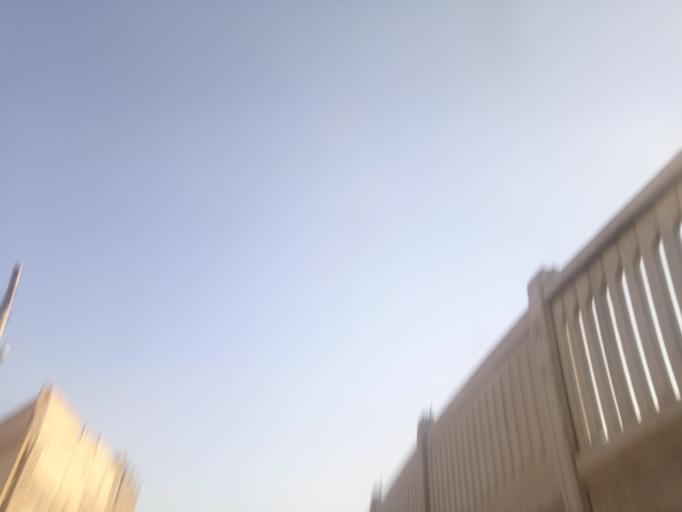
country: IR
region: Qom
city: Qom
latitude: 34.6642
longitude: 50.8681
